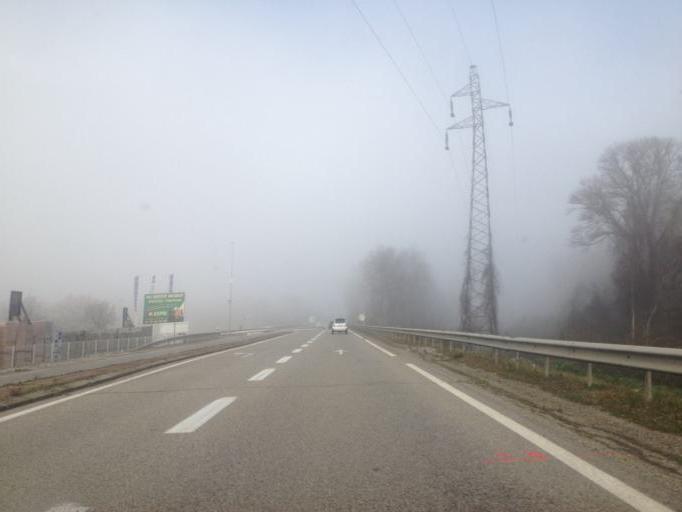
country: FR
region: Rhone-Alpes
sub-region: Departement de l'Ardeche
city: Le Teil
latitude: 44.5418
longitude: 4.6919
